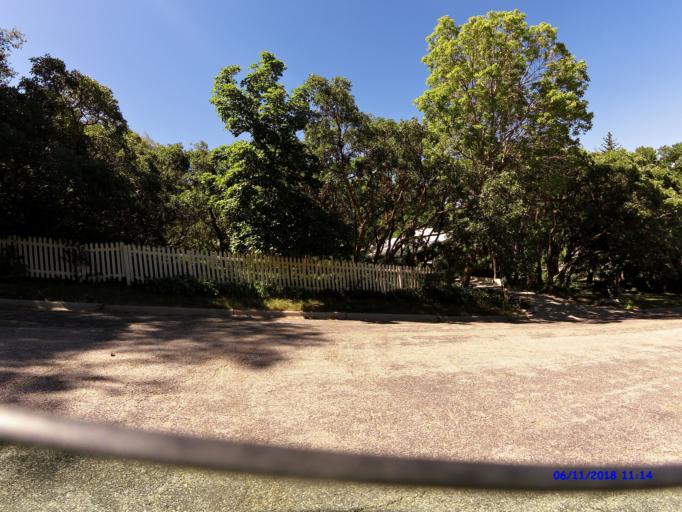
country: US
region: Utah
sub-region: Weber County
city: Ogden
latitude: 41.2202
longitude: -111.9327
